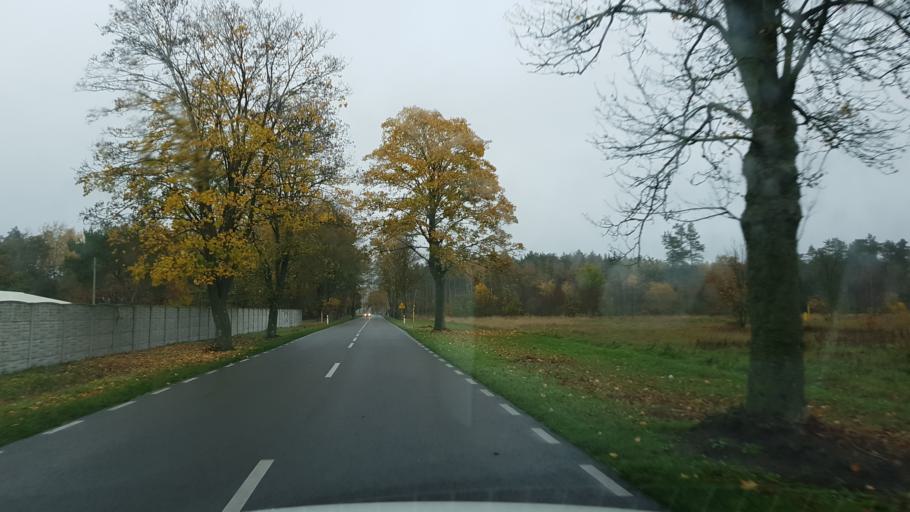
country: PL
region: West Pomeranian Voivodeship
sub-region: Powiat goleniowski
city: Goleniow
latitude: 53.6093
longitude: 14.7405
